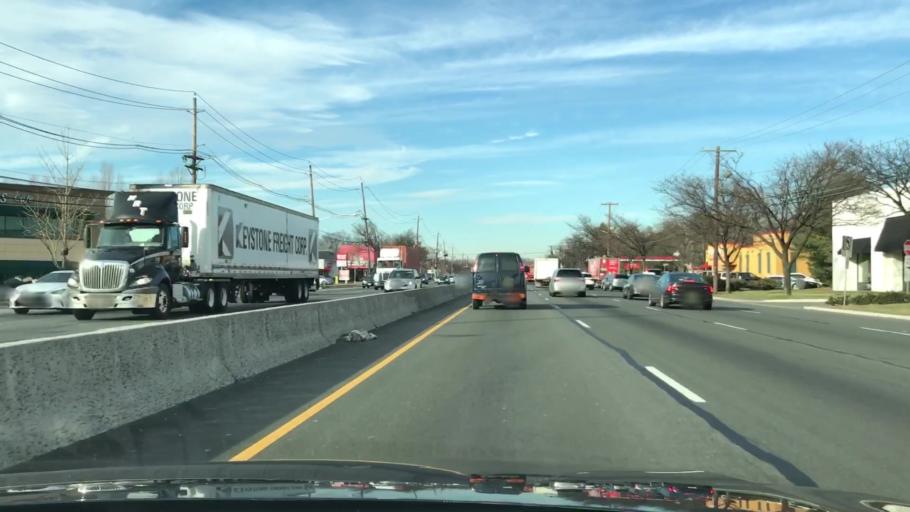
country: US
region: New Jersey
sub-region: Bergen County
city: Paramus
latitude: 40.9726
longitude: -74.0805
